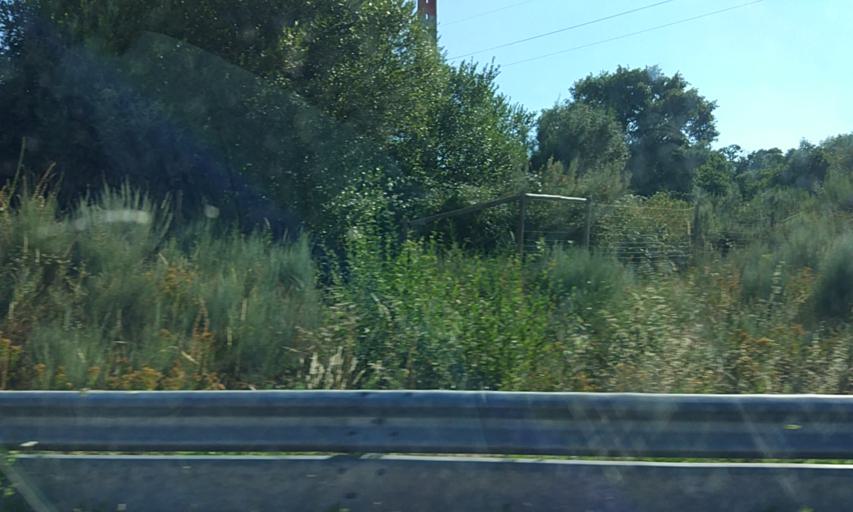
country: PT
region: Braganca
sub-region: Braganca Municipality
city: Braganca
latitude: 41.6753
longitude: -6.8143
